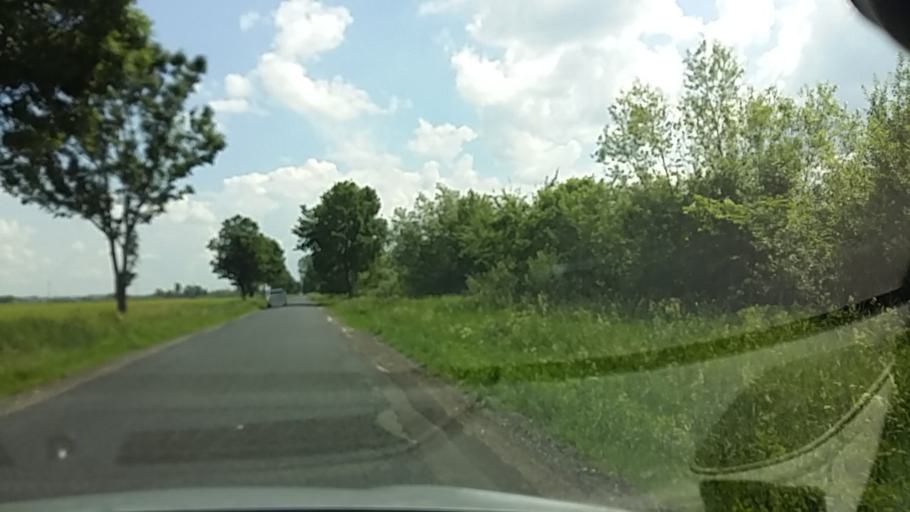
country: HU
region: Vas
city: Kormend
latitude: 46.9657
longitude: 16.5283
